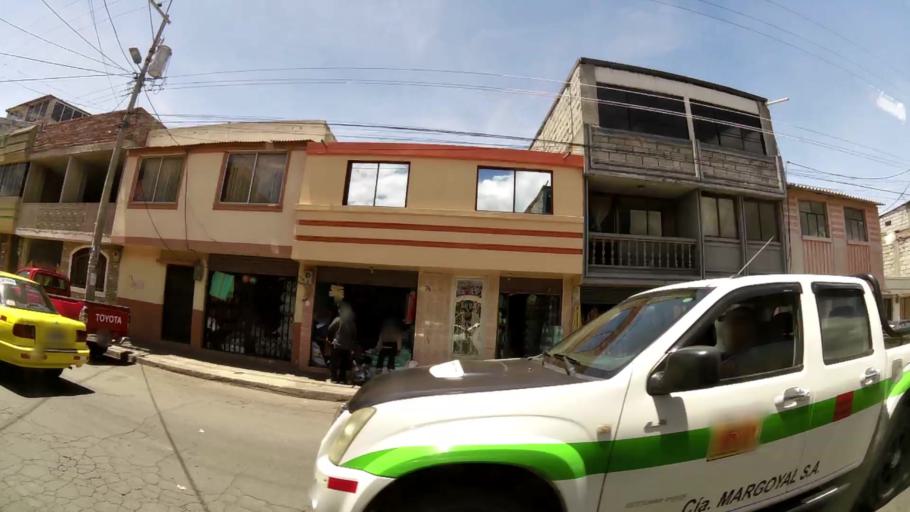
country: EC
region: Chimborazo
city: Riobamba
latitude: -1.6838
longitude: -78.6352
